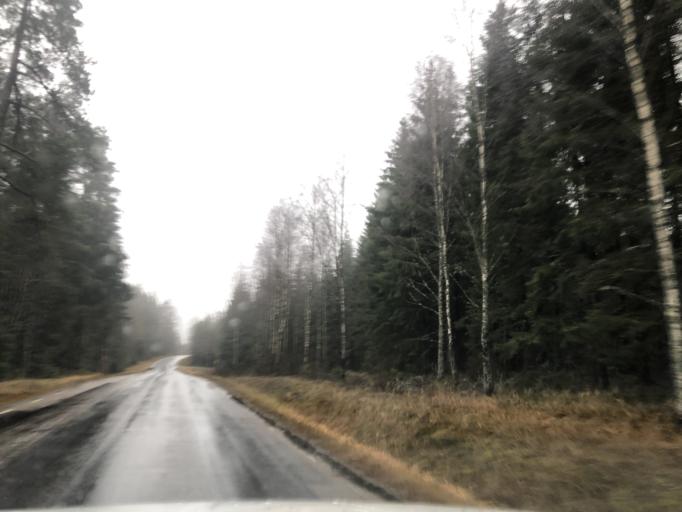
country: SE
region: Vaestra Goetaland
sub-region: Ulricehamns Kommun
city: Ulricehamn
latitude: 57.8385
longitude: 13.5351
